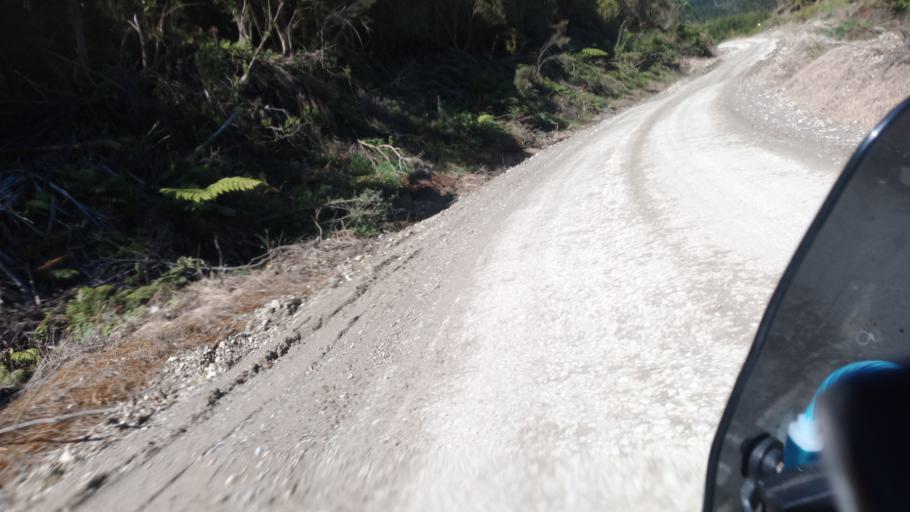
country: NZ
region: Gisborne
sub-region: Gisborne District
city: Gisborne
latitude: -38.8850
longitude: 177.7844
